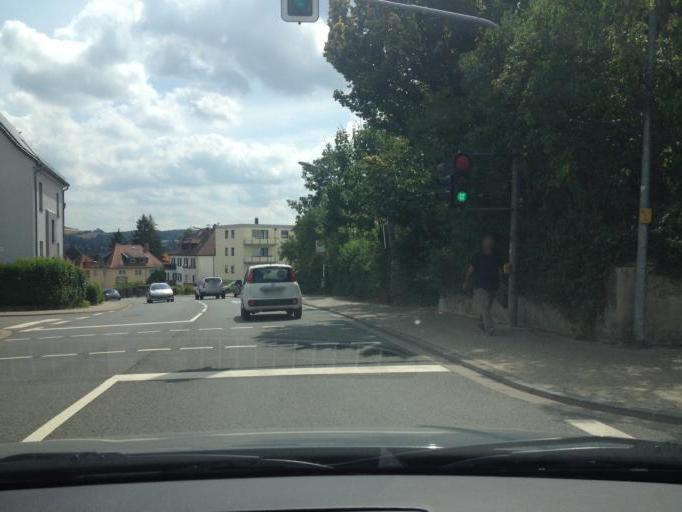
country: DE
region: Saarland
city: Sankt Wendel
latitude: 49.4672
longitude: 7.1591
